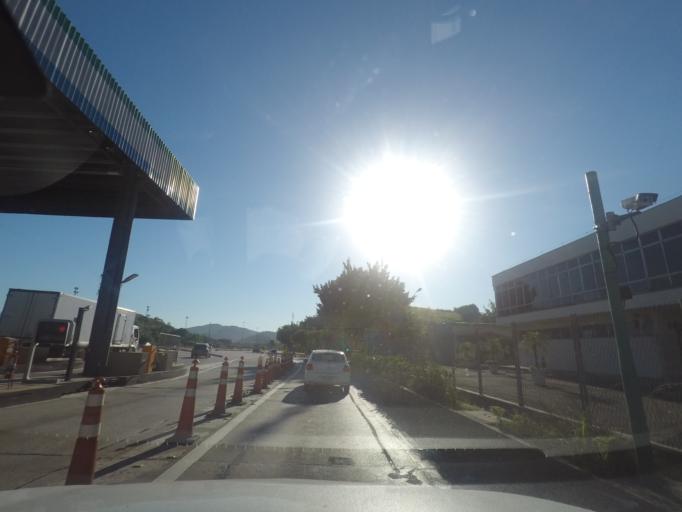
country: BR
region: Rio de Janeiro
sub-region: Petropolis
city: Petropolis
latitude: -22.6475
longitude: -43.1881
